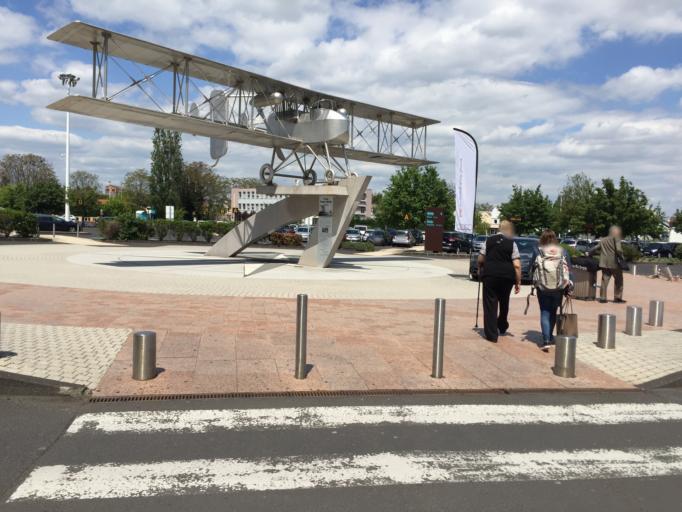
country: FR
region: Auvergne
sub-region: Departement du Puy-de-Dome
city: Aulnat
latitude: 45.7902
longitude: 3.1600
